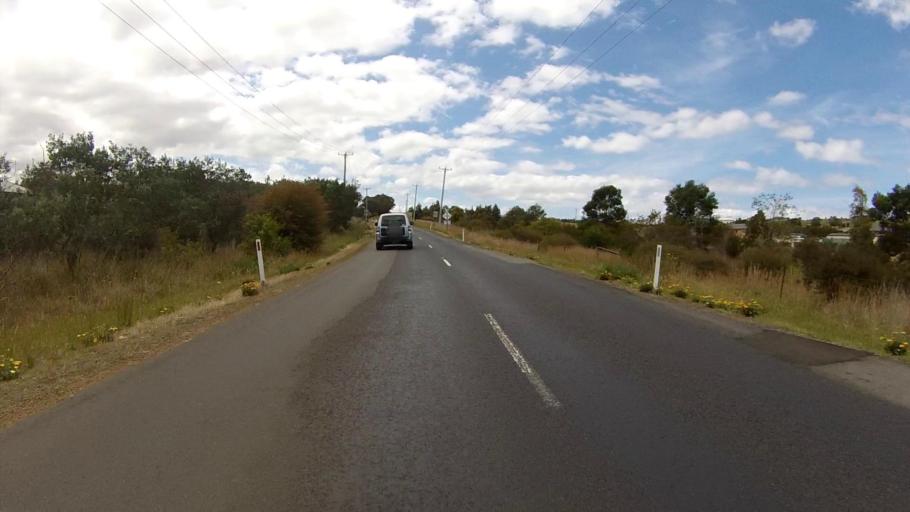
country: AU
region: Tasmania
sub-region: Sorell
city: Sorell
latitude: -42.8185
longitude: 147.6119
